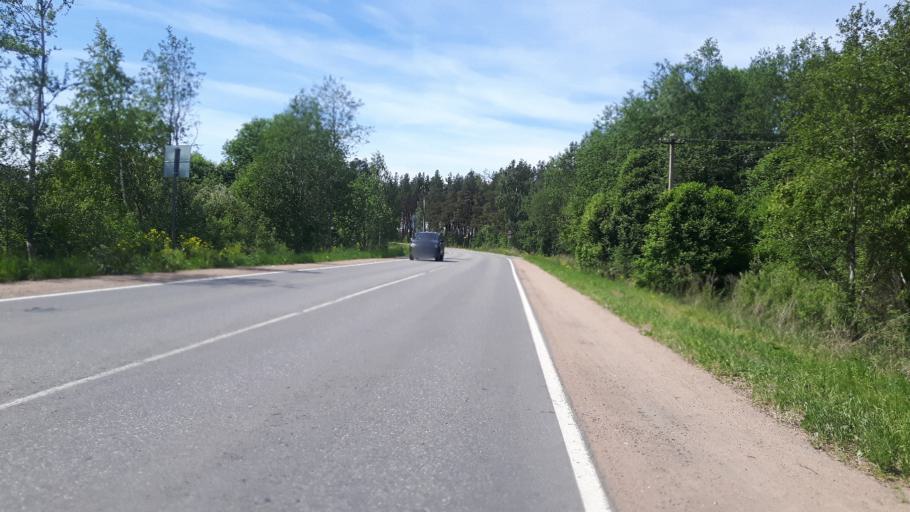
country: RU
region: Leningrad
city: Ust'-Luga
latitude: 59.5710
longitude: 28.1641
